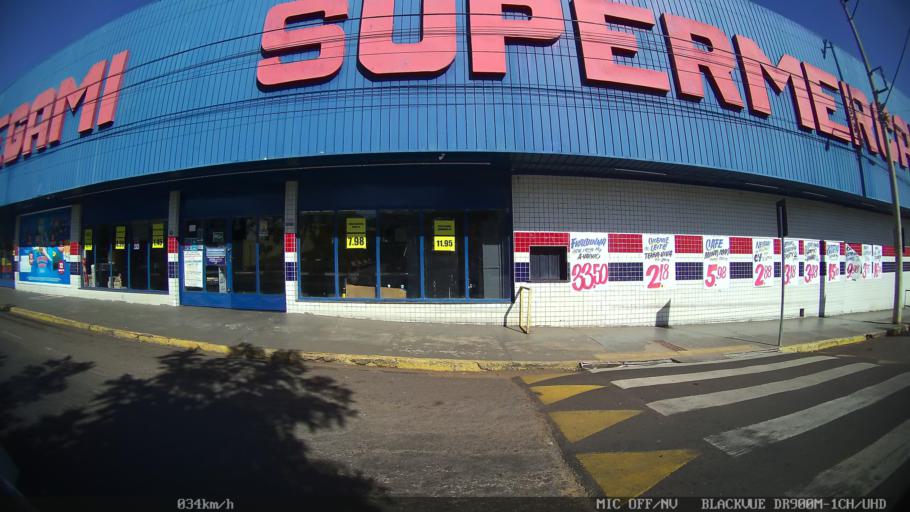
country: BR
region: Sao Paulo
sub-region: Olimpia
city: Olimpia
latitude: -20.7400
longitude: -48.9065
